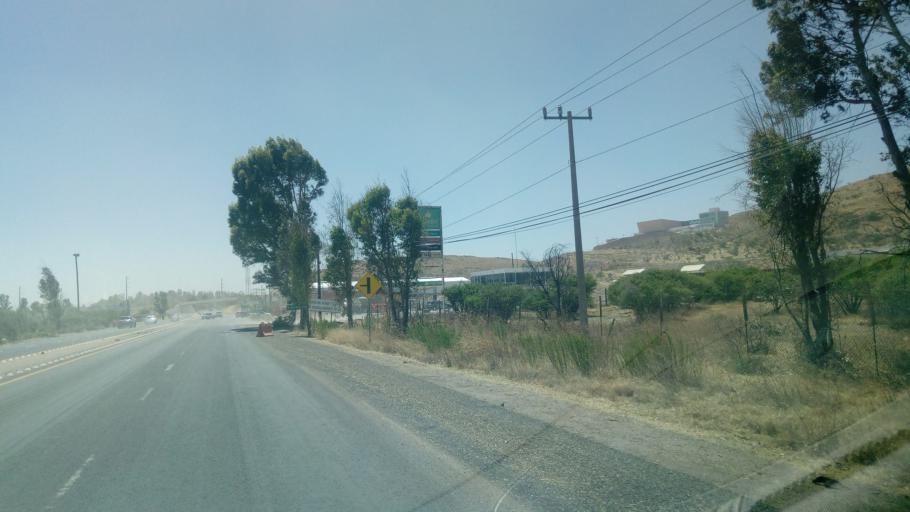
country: MX
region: Durango
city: Victoria de Durango
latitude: 24.0730
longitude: -104.6594
